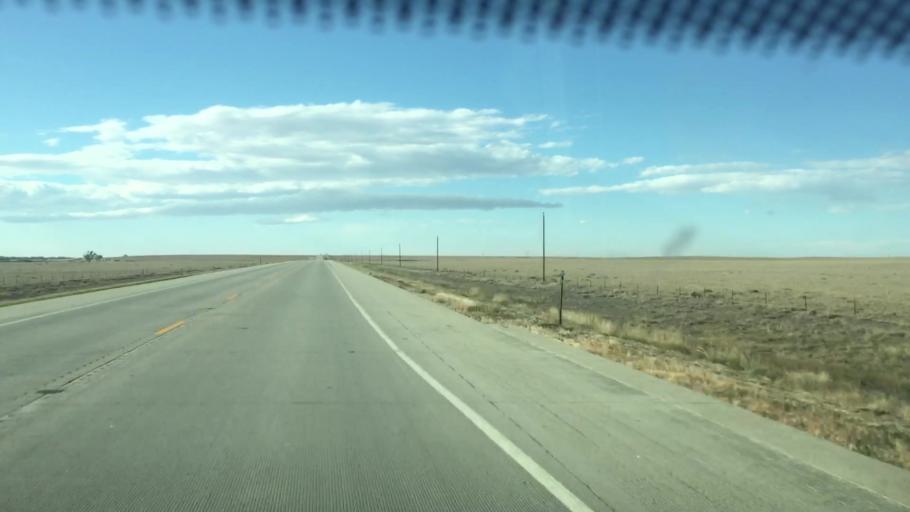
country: US
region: Colorado
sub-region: Lincoln County
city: Hugo
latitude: 39.0565
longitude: -103.3568
